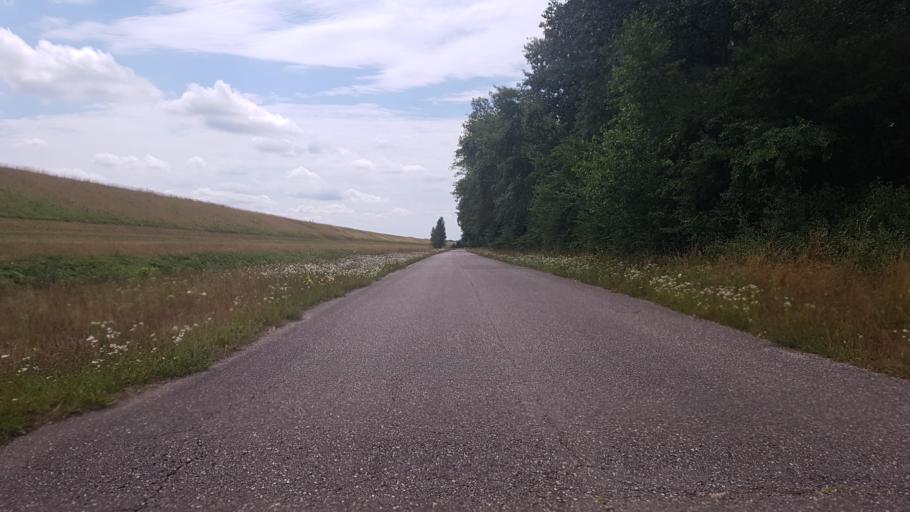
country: DE
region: Baden-Wuerttemberg
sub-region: Karlsruhe Region
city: Hugelsheim
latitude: 48.8116
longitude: 8.0944
